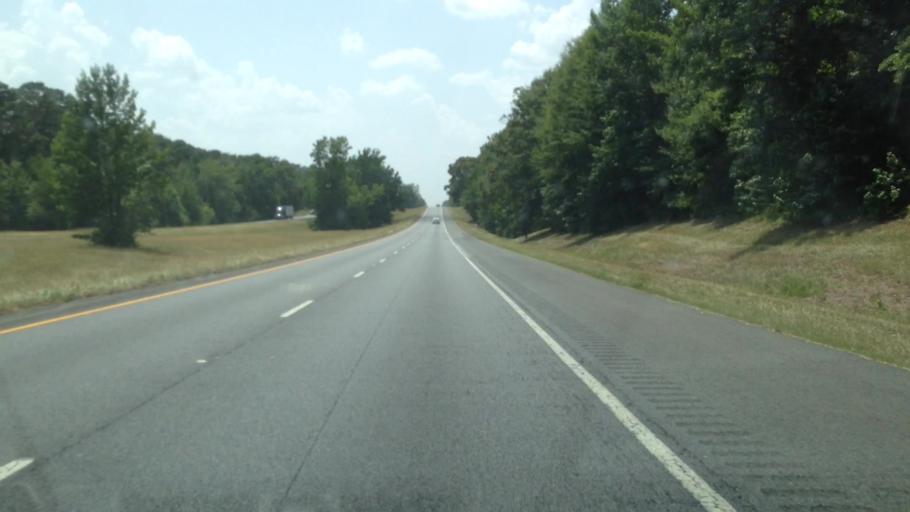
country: US
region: Louisiana
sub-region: Lincoln Parish
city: Grambling
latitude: 32.5450
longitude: -92.7462
